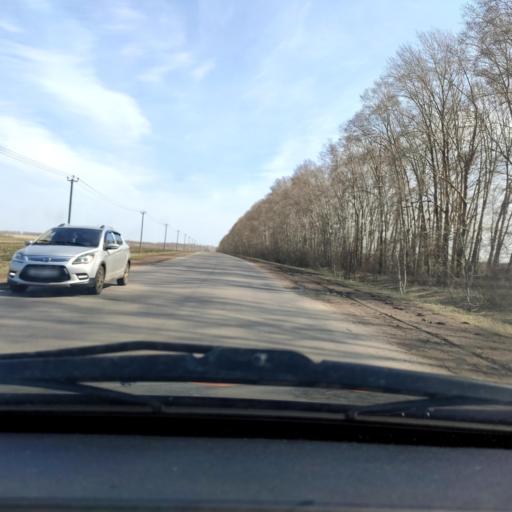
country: RU
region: Bashkortostan
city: Asanovo
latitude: 54.8182
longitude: 55.6043
